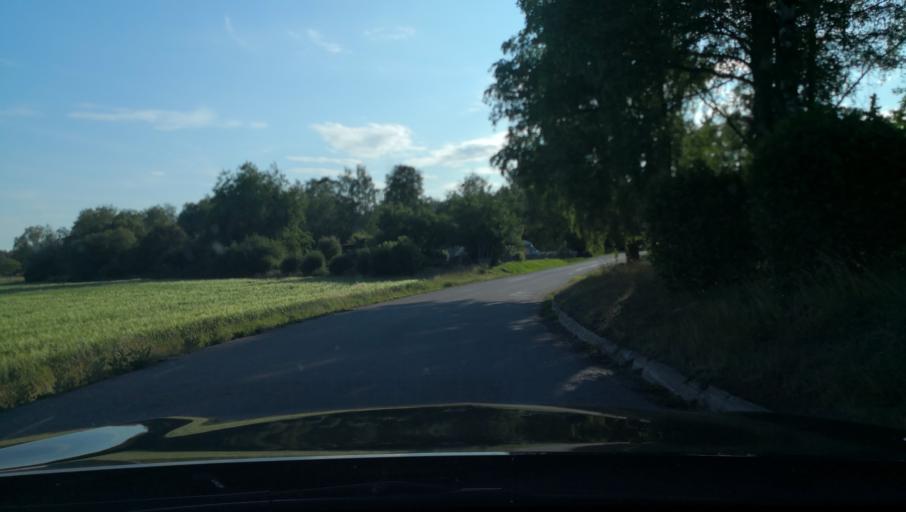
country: SE
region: Uppsala
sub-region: Osthammars Kommun
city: Osterbybruk
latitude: 60.0202
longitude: 17.9618
